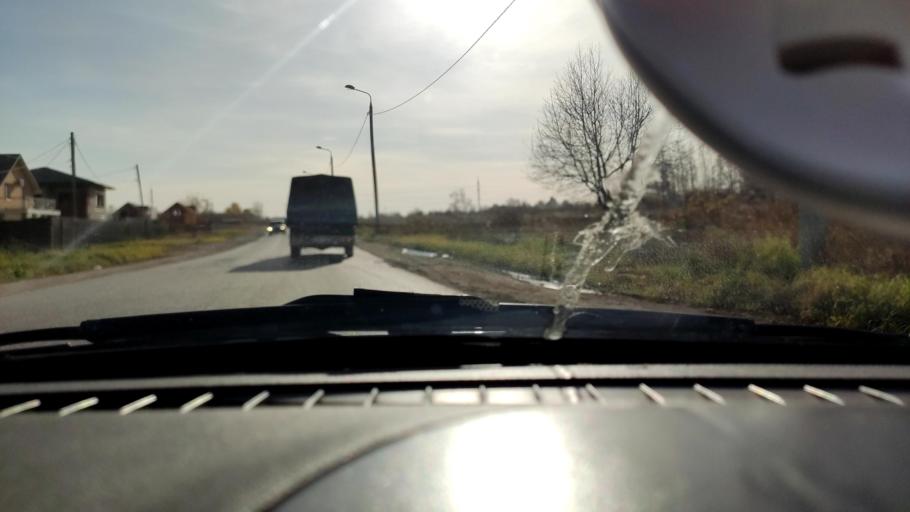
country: RU
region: Perm
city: Perm
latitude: 58.0215
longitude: 56.3349
